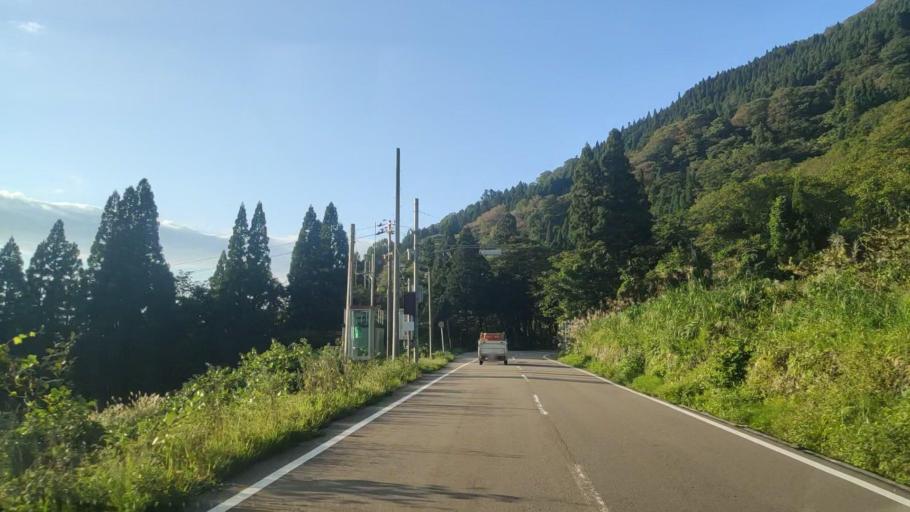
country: JP
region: Toyama
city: Yatsuomachi-higashikumisaka
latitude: 36.4972
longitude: 137.0262
